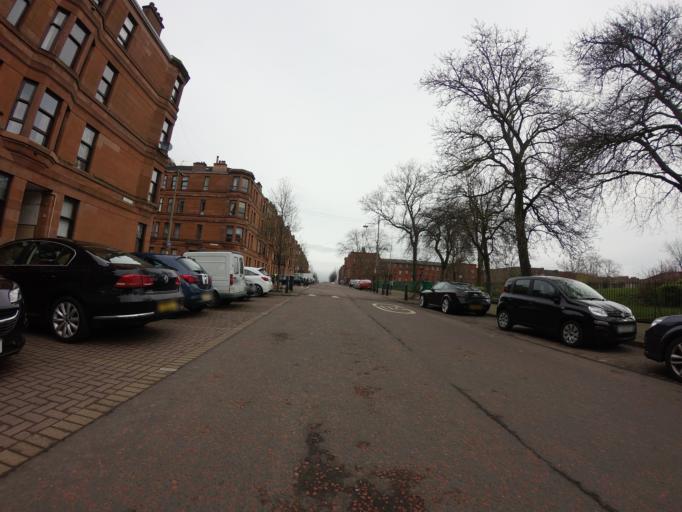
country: GB
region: Scotland
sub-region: Glasgow City
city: Glasgow
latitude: 55.8387
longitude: -4.2608
